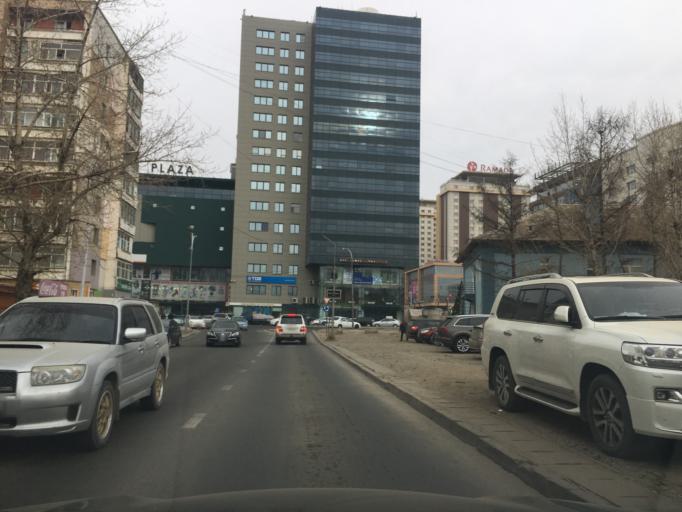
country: MN
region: Ulaanbaatar
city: Ulaanbaatar
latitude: 47.9131
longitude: 106.8906
